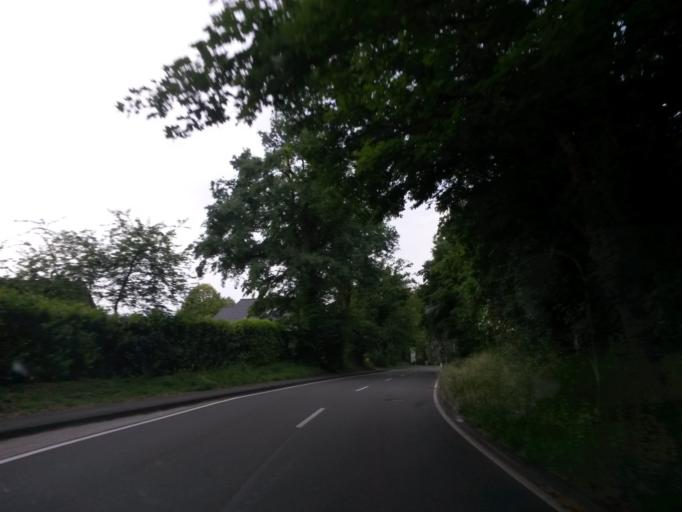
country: DE
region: North Rhine-Westphalia
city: Lohmar
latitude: 50.8593
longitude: 7.2225
